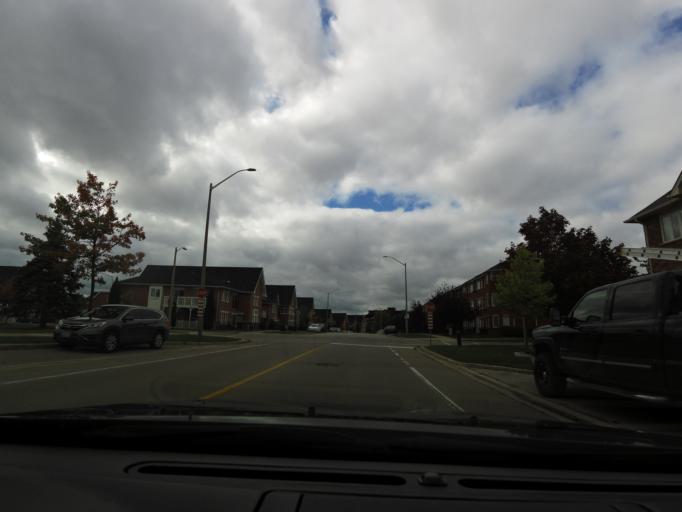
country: CA
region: Ontario
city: Burlington
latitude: 43.3927
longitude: -79.7809
